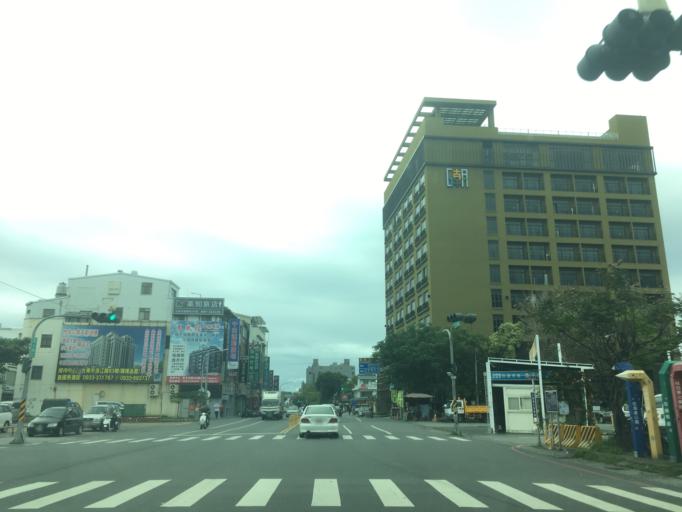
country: TW
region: Taiwan
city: Taitung City
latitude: 22.7555
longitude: 121.1448
